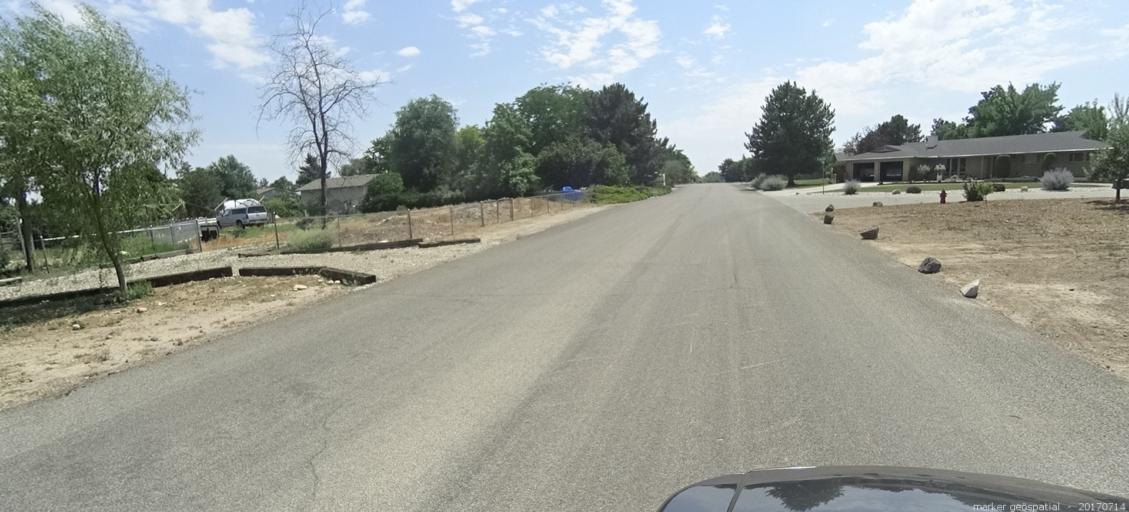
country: US
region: Idaho
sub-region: Ada County
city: Meridian
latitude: 43.5367
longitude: -116.3244
